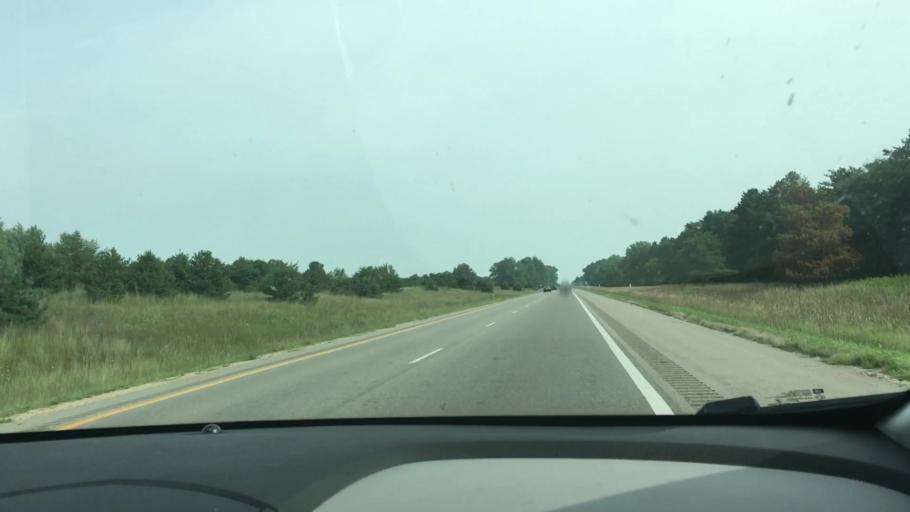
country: US
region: Michigan
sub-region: Kalamazoo County
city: Schoolcraft
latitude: 42.1608
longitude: -85.6440
